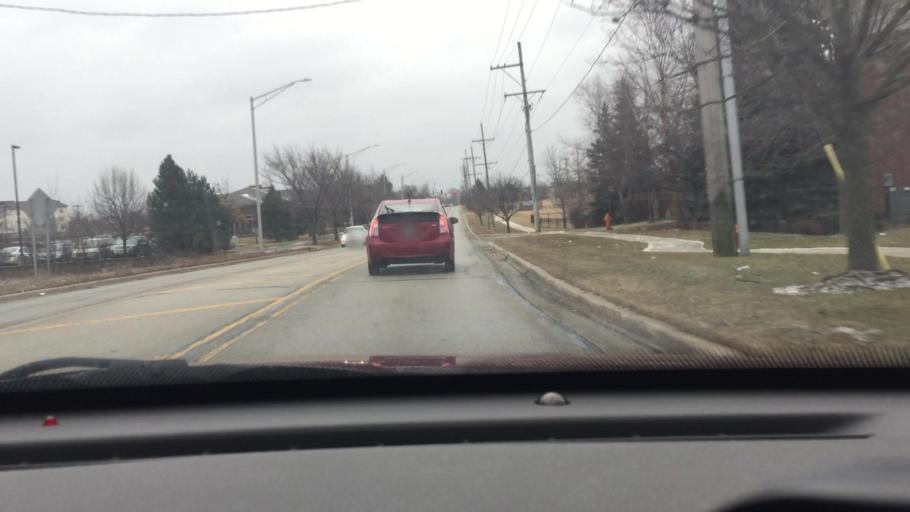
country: US
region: Illinois
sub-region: DuPage County
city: Naperville
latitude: 41.7839
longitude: -88.1819
